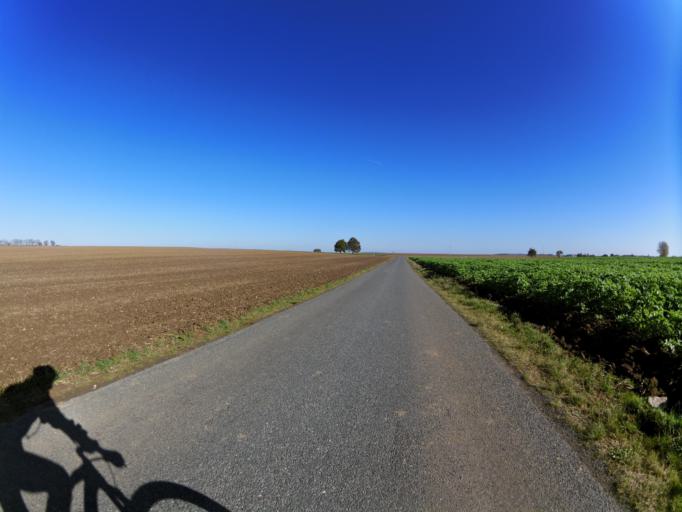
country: DE
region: Bavaria
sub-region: Regierungsbezirk Unterfranken
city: Sulzdorf
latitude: 49.6663
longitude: 9.9191
